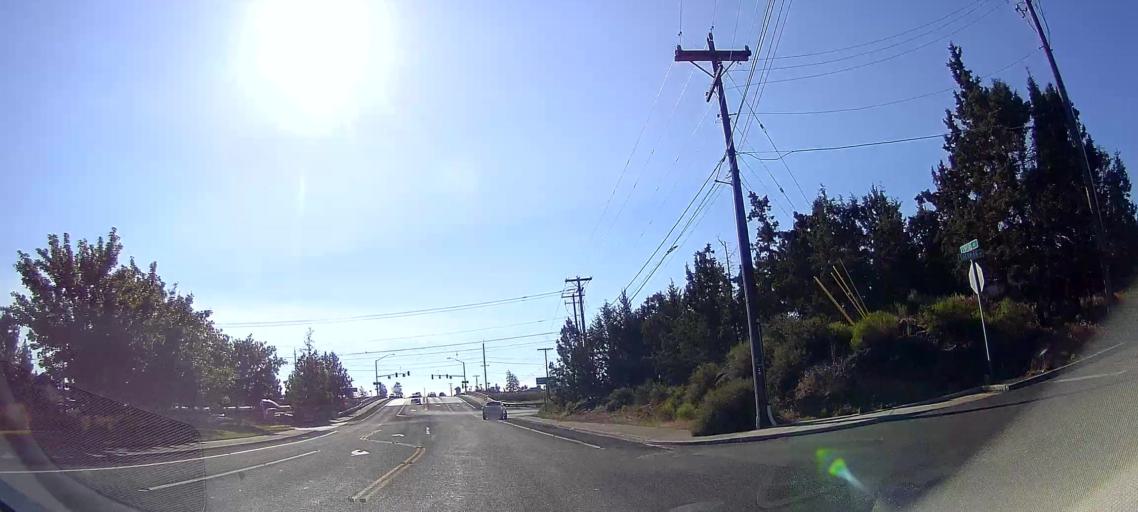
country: US
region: Oregon
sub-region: Deschutes County
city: Bend
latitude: 44.0912
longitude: -121.3033
